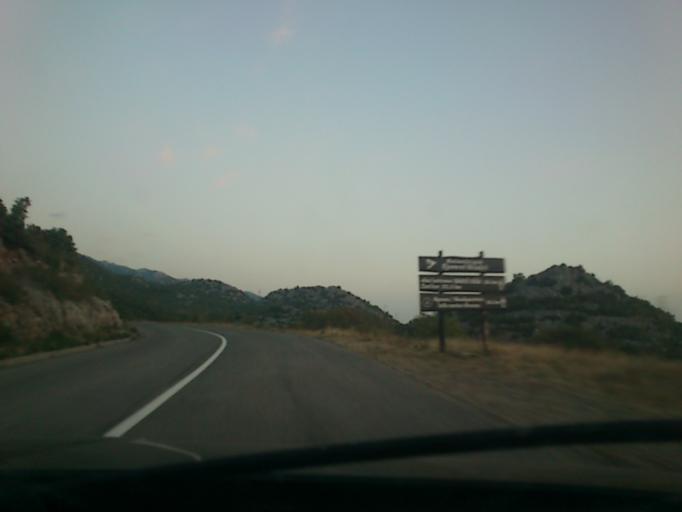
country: HR
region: Licko-Senjska
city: Senj
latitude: 44.9233
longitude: 14.9174
